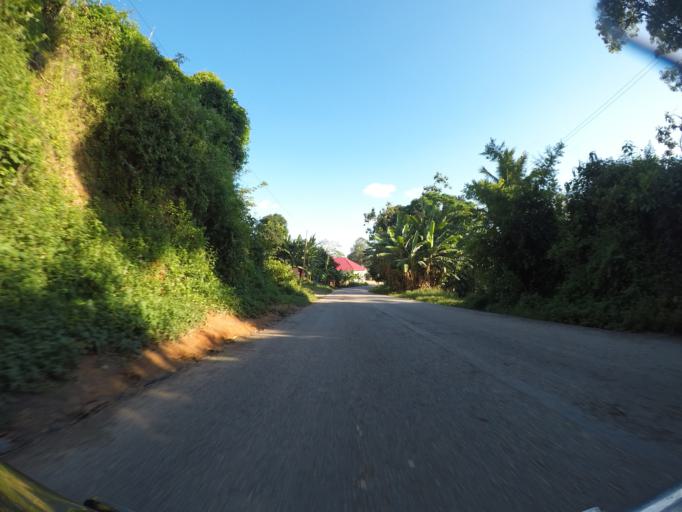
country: TZ
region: Pemba South
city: Mtambile
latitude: -5.3358
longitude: 39.7302
